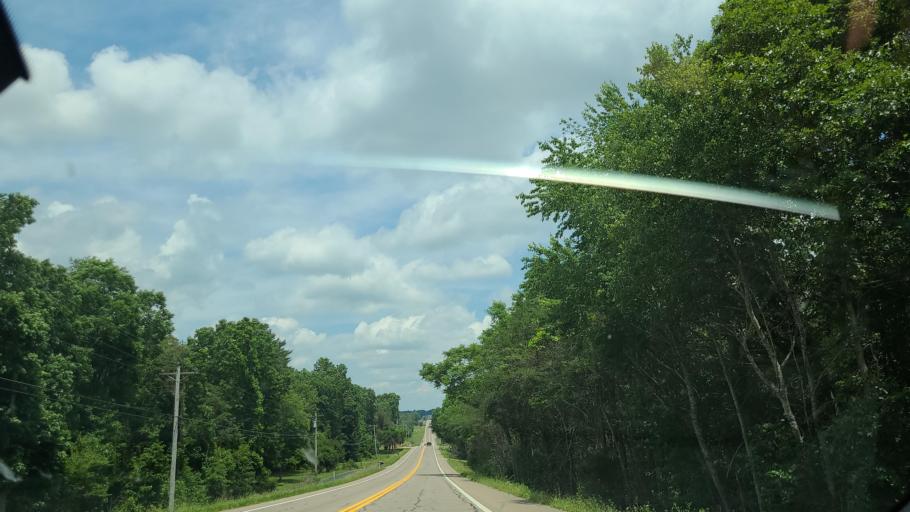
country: US
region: Tennessee
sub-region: Cumberland County
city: Lake Tansi
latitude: 35.8460
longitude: -85.0153
